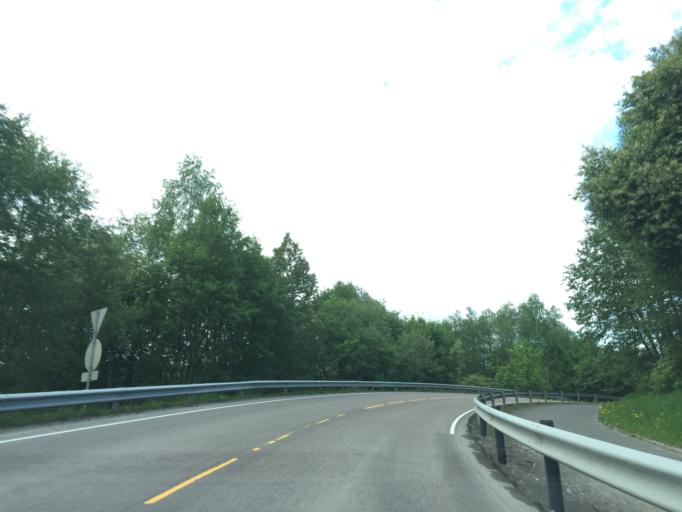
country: NO
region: Akershus
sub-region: Fet
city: Fetsund
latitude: 59.9242
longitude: 11.1700
